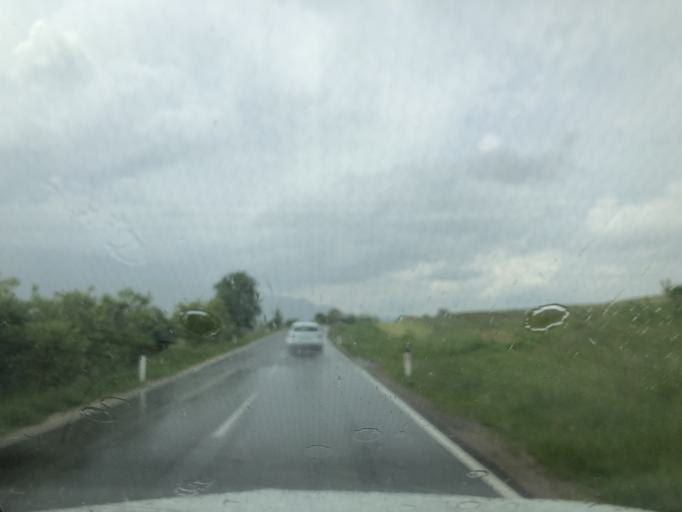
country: SI
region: Cerknica
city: Cerknica
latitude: 45.7738
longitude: 14.4105
